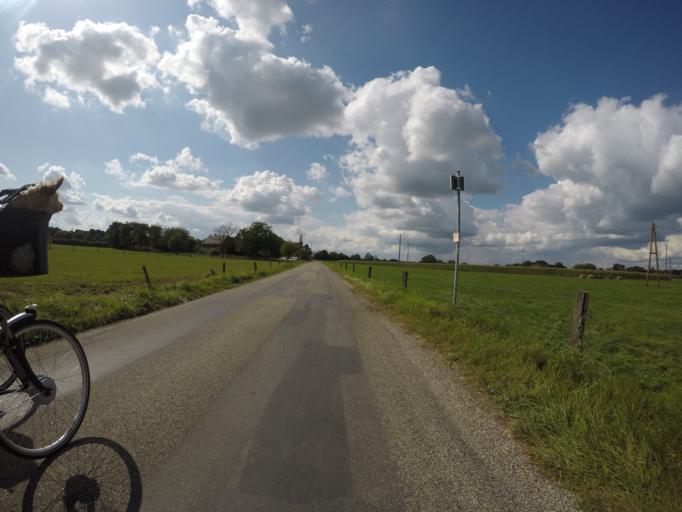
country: DE
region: North Rhine-Westphalia
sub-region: Regierungsbezirk Dusseldorf
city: Mehrhoog
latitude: 51.7695
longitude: 6.5236
